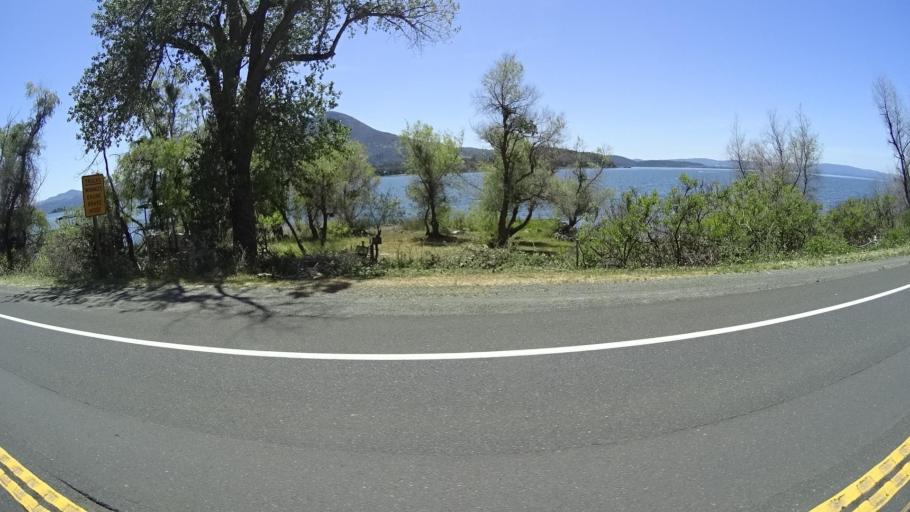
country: US
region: California
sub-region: Lake County
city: Soda Bay
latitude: 39.0324
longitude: -122.7418
